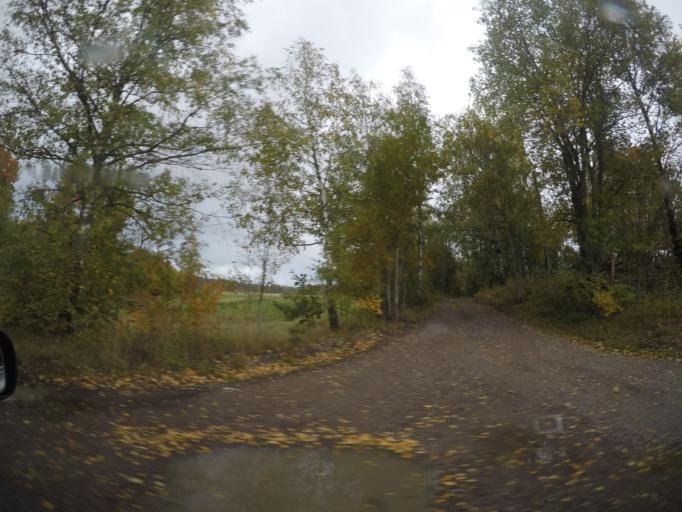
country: SE
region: Soedermanland
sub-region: Eskilstuna Kommun
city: Kvicksund
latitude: 59.3271
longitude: 16.3004
